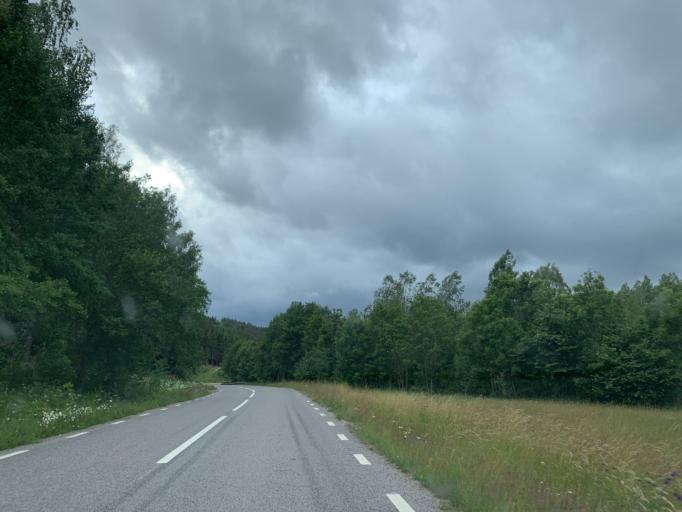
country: SE
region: Kalmar
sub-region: Vasterviks Kommun
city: Overum
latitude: 58.0171
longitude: 16.1595
